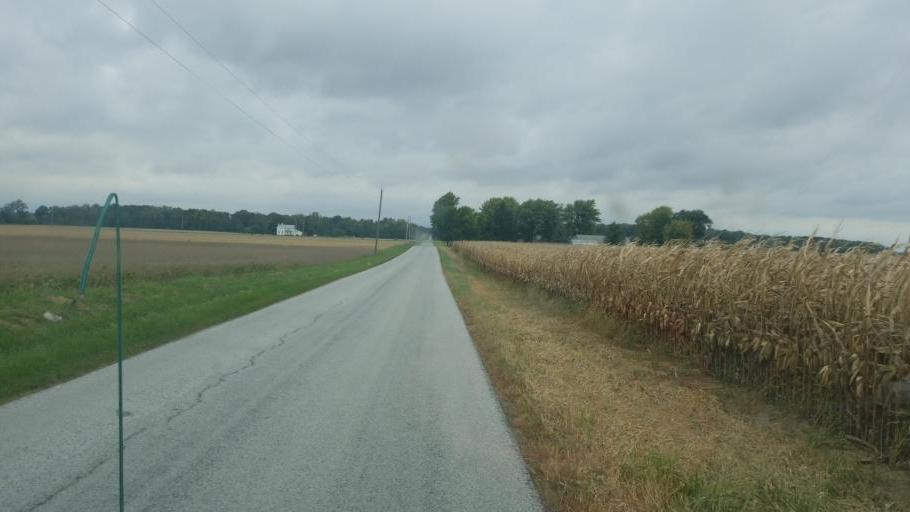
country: US
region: Ohio
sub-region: Seneca County
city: Fostoria
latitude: 41.0637
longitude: -83.4961
